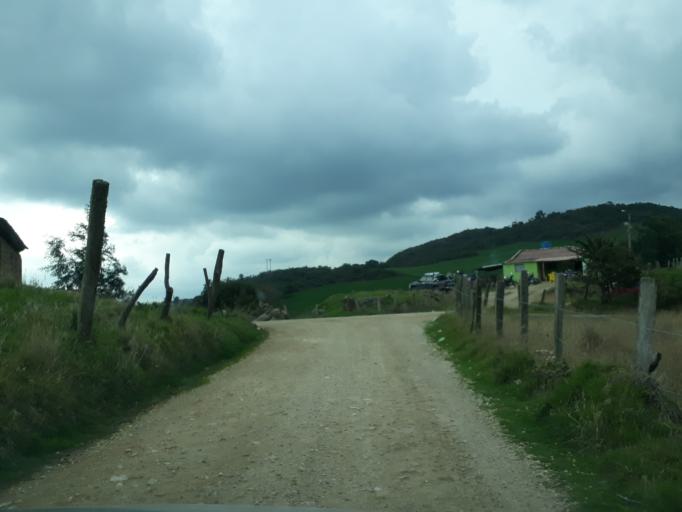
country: CO
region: Cundinamarca
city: Lenguazaque
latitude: 5.2875
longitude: -73.6825
